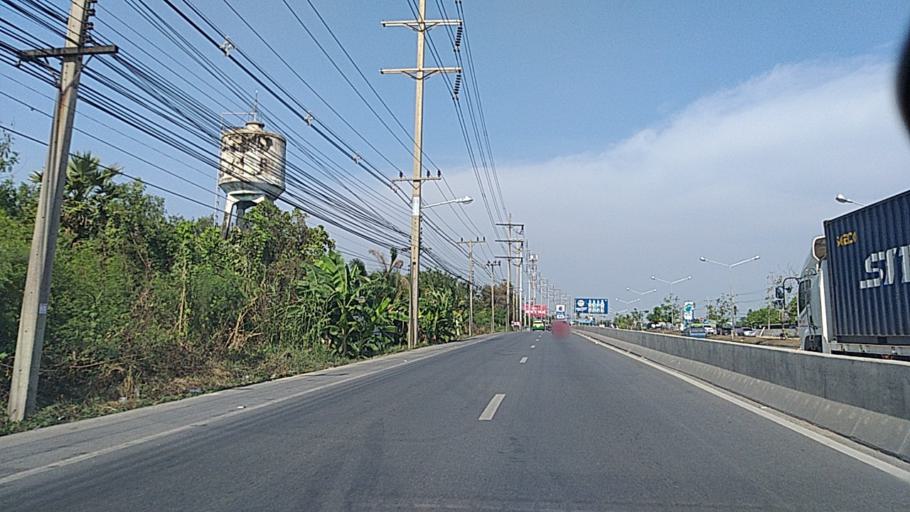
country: TH
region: Nakhon Pathom
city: Sam Phran
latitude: 13.7844
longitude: 100.2503
